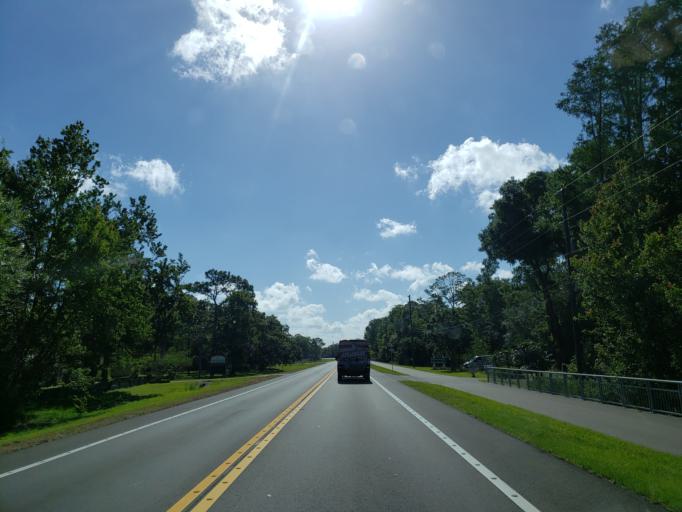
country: US
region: Florida
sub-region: Pasco County
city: Trinity
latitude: 28.1441
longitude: -82.6680
